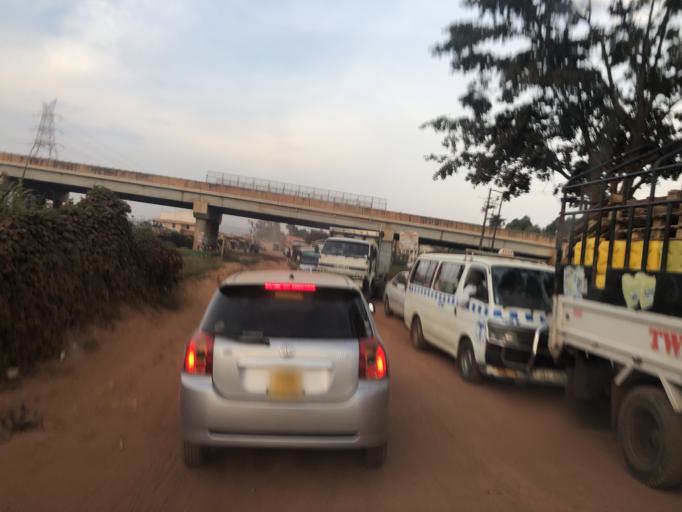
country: UG
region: Central Region
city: Kampala Central Division
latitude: 0.3001
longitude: 32.5117
